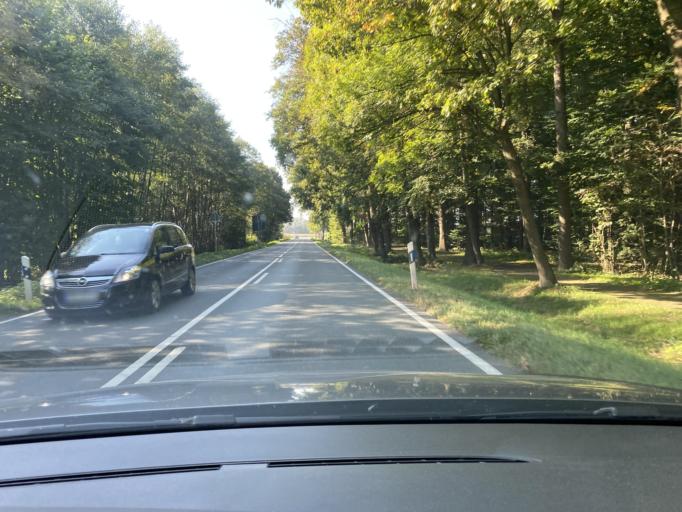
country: DE
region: North Rhine-Westphalia
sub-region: Regierungsbezirk Munster
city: Heek
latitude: 52.1180
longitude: 7.1484
